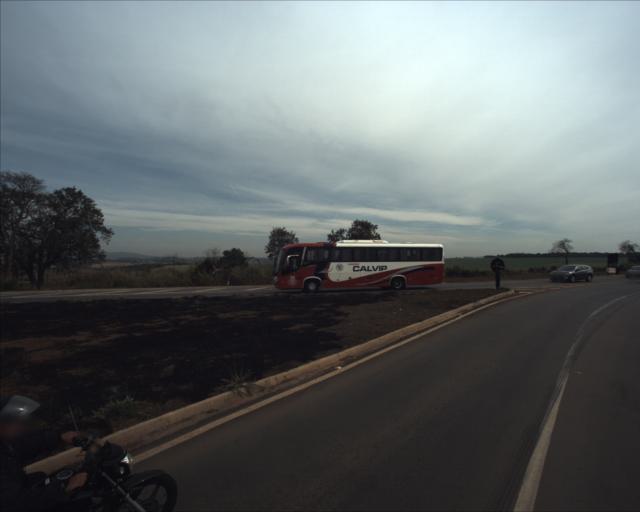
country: BR
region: Sao Paulo
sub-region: Sorocaba
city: Sorocaba
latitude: -23.4173
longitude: -47.5205
